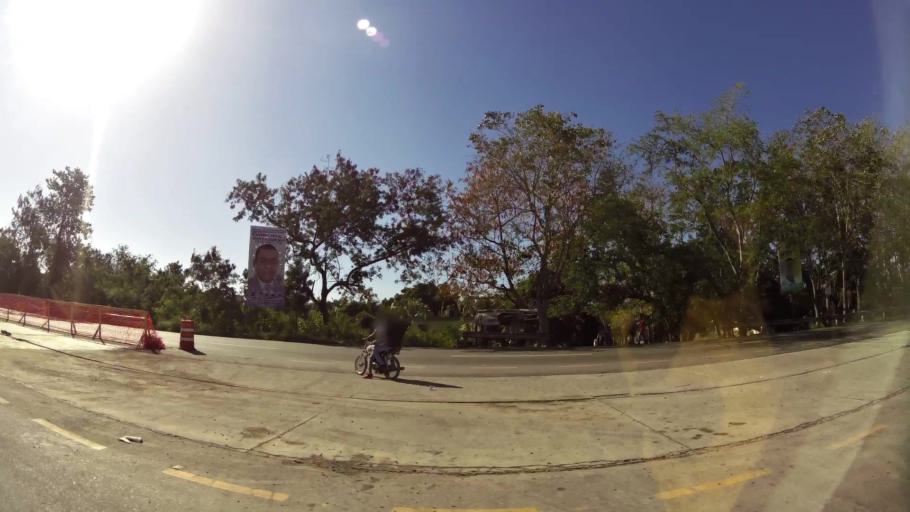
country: DO
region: San Cristobal
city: El Carril
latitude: 18.4383
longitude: -70.0116
